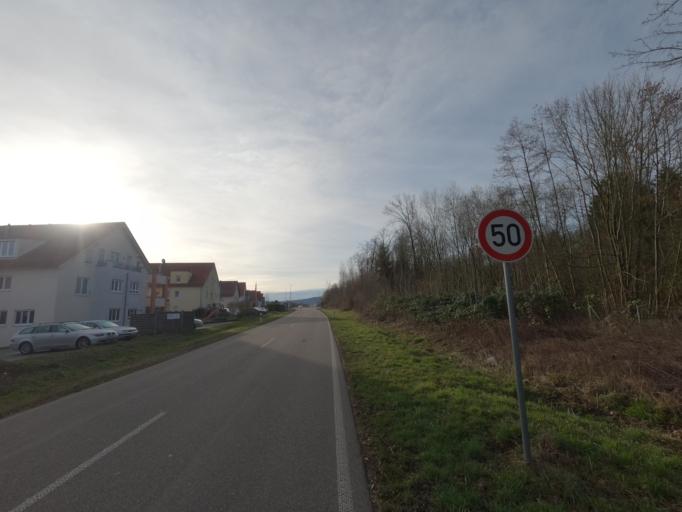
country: DE
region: Baden-Wuerttemberg
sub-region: Regierungsbezirk Stuttgart
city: Uhingen
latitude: 48.6972
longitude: 9.5809
